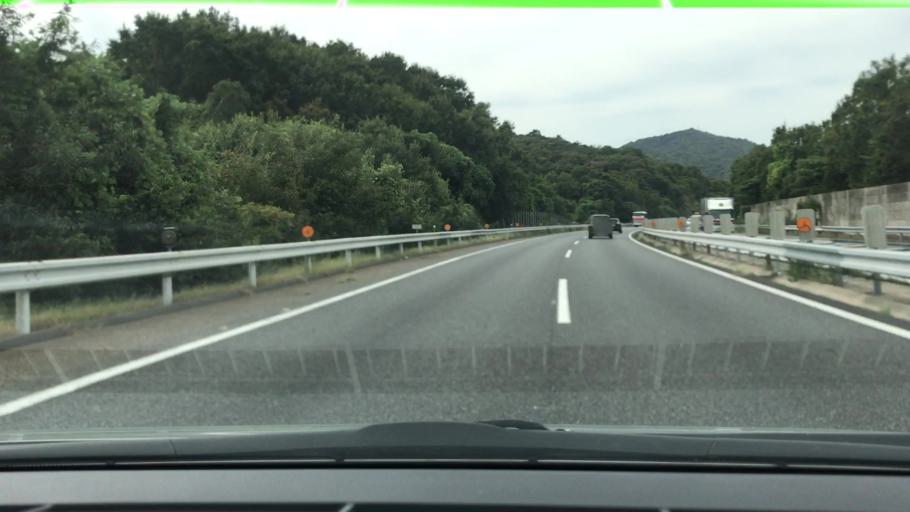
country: JP
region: Hyogo
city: Aioi
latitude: 34.8110
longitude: 134.4555
